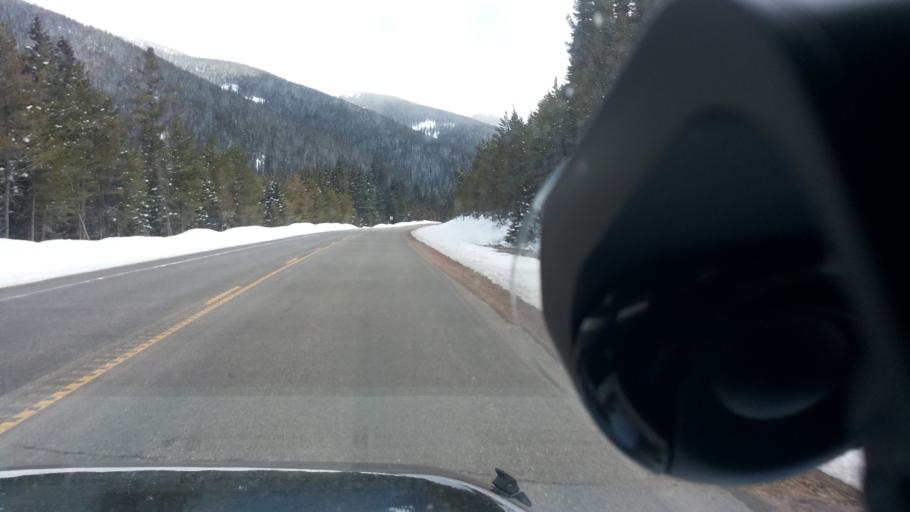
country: US
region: Colorado
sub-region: Grand County
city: Fraser
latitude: 39.8517
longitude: -105.7524
